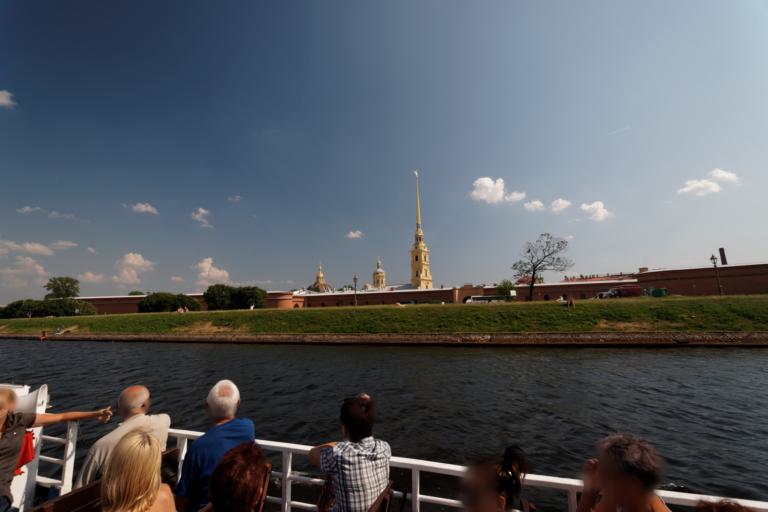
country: RU
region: St.-Petersburg
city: Saint Petersburg
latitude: 59.9516
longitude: 30.3122
